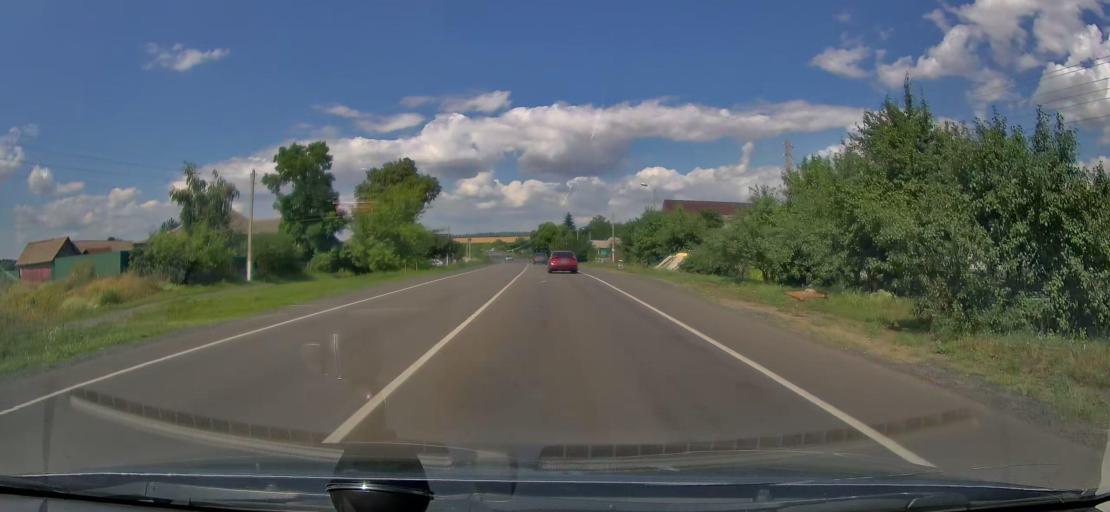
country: RU
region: Kursk
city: Zolotukhino
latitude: 51.9346
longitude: 36.3090
